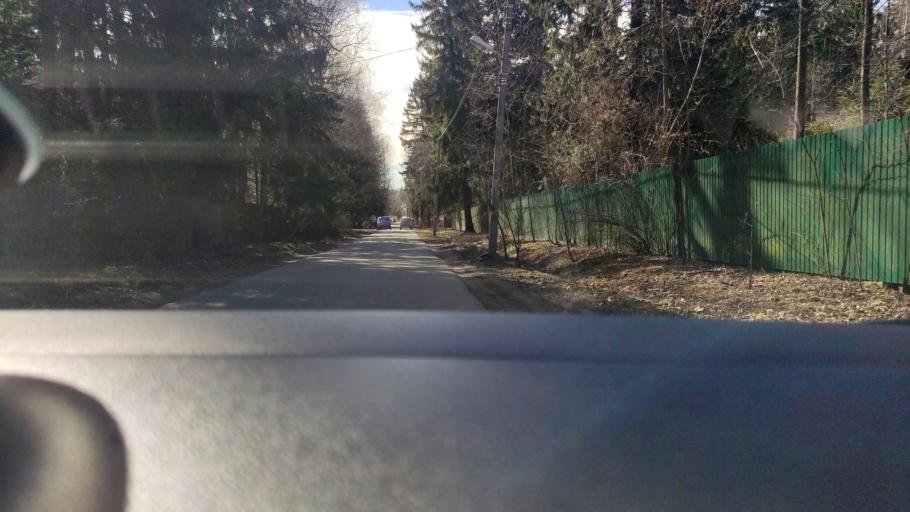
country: RU
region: Moskovskaya
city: Aprelevka
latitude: 55.5409
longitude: 37.0509
